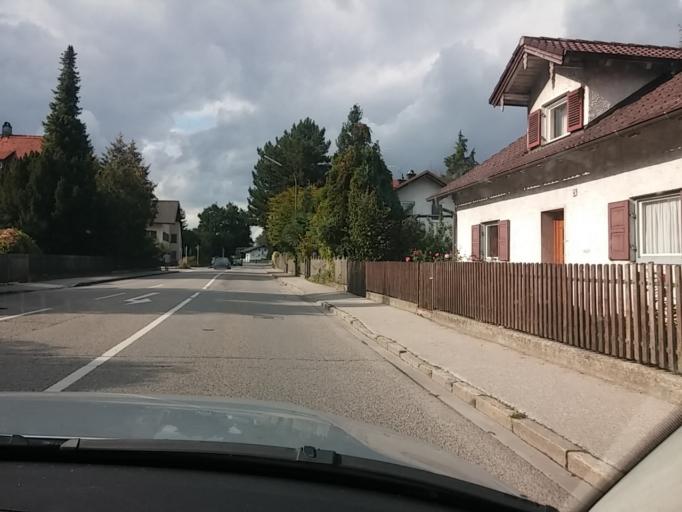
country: DE
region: Bavaria
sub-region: Upper Bavaria
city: Grafing bei Munchen
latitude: 48.0476
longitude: 11.9673
